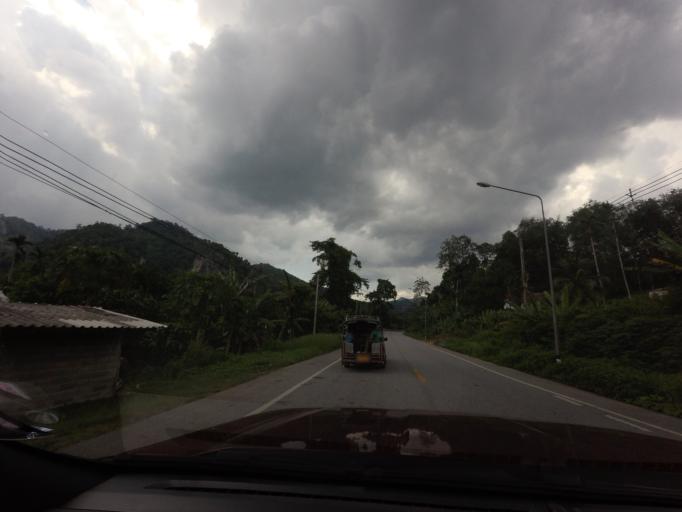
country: TH
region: Yala
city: Than To
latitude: 6.2228
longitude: 101.1653
